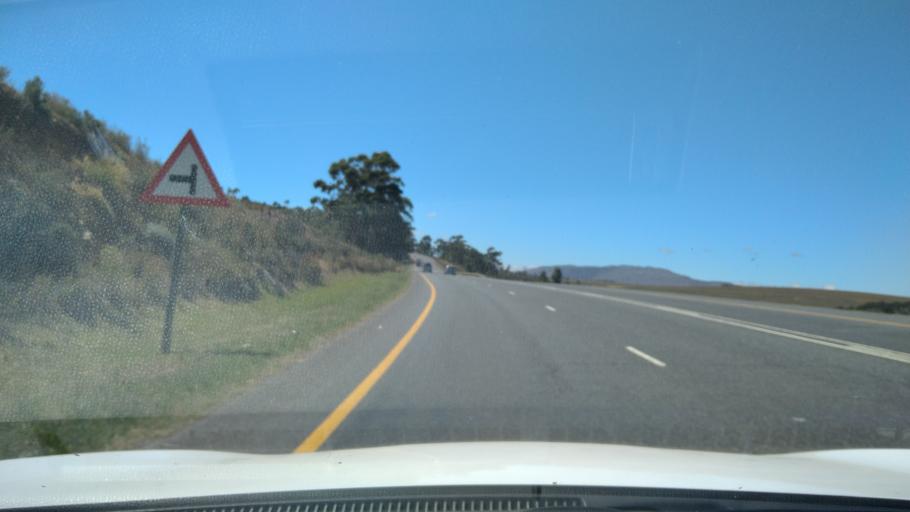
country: ZA
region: Western Cape
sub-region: Overberg District Municipality
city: Caledon
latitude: -34.2160
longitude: 19.4014
